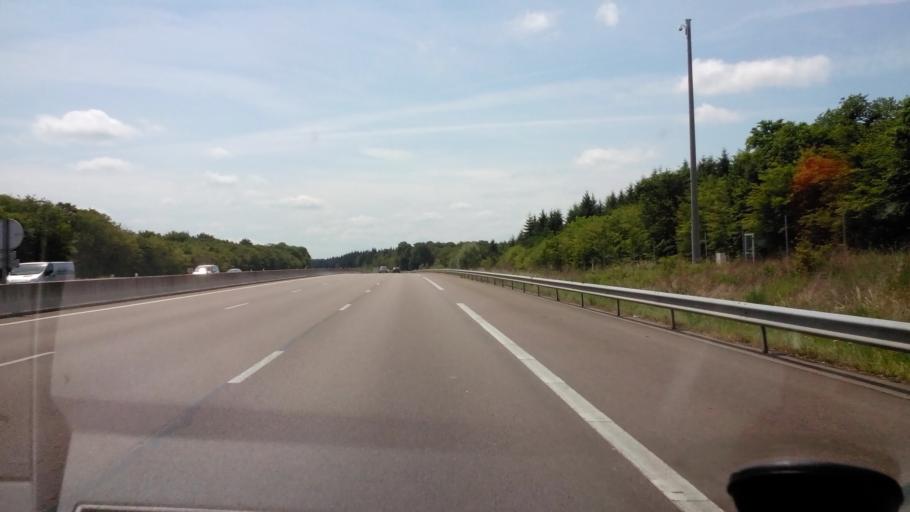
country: FR
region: Bourgogne
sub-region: Departement de la Cote-d'Or
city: Selongey
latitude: 47.6747
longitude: 5.1770
